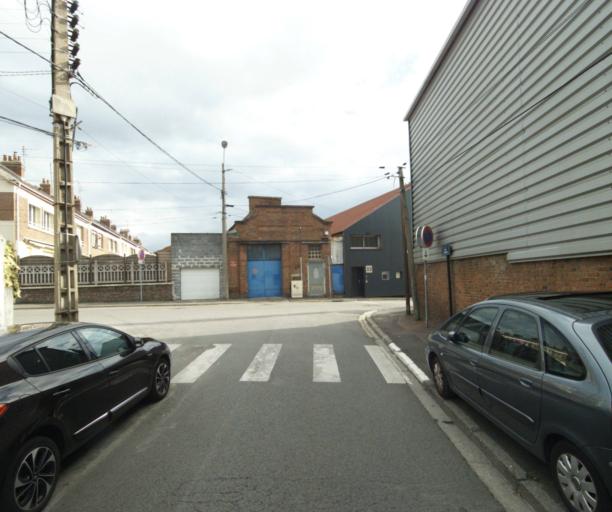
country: FR
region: Nord-Pas-de-Calais
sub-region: Departement du Nord
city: Saint-Andre-lez-Lille
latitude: 50.6535
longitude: 3.0582
